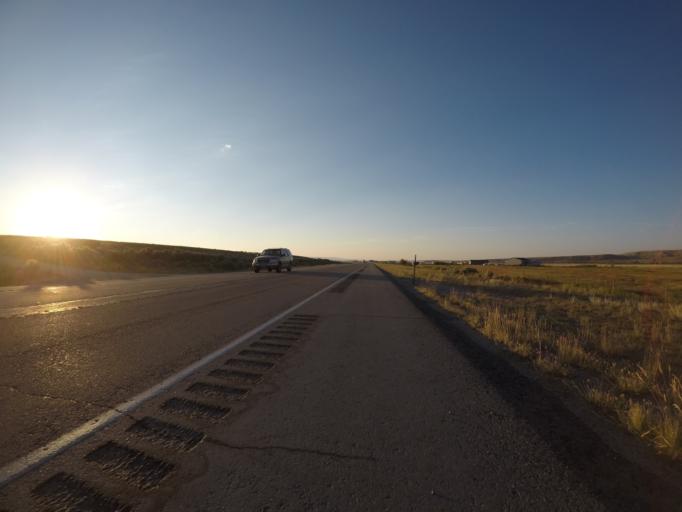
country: US
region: Wyoming
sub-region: Sublette County
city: Pinedale
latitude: 42.8066
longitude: -109.8220
